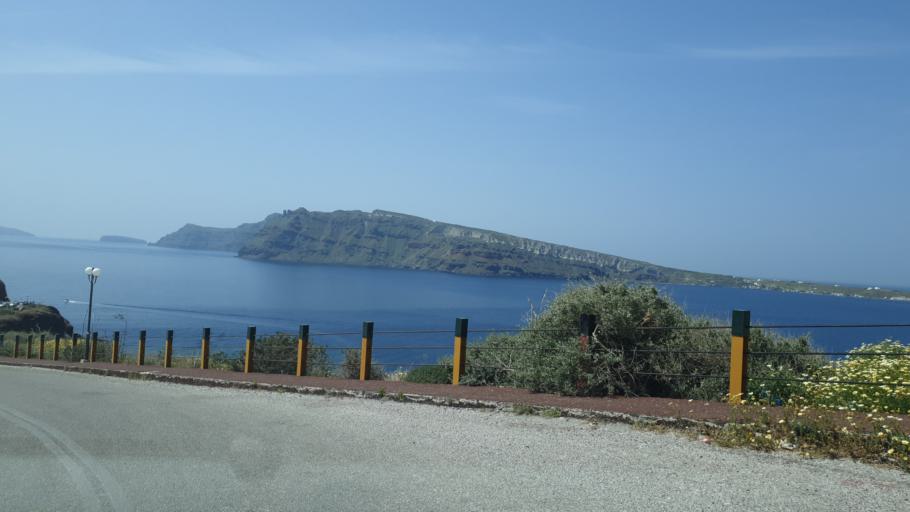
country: GR
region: South Aegean
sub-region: Nomos Kykladon
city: Oia
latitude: 36.4646
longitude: 25.3700
